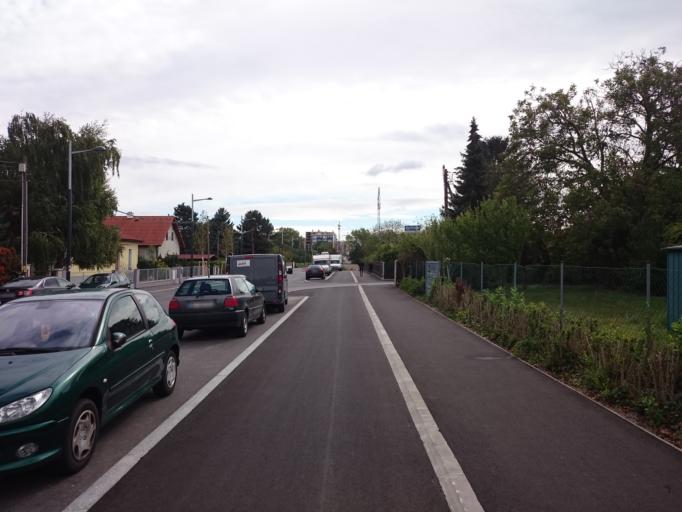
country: AT
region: Lower Austria
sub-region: Politischer Bezirk Ganserndorf
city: Gross-Enzersdorf
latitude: 48.2259
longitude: 16.4920
